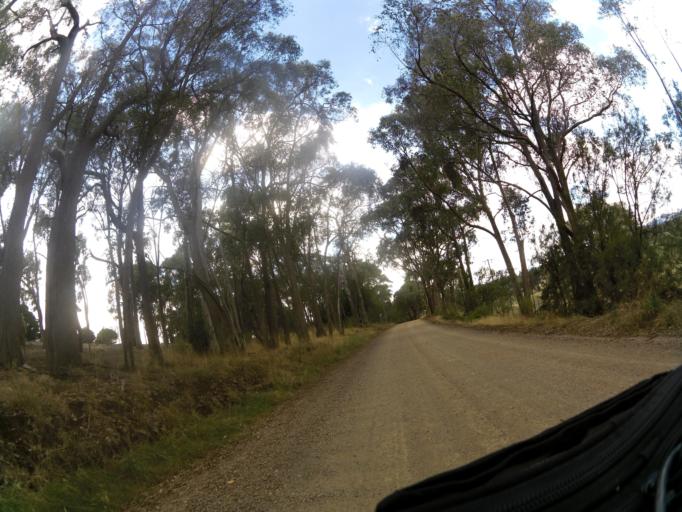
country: AU
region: Victoria
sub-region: Benalla
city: Benalla
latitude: -36.7819
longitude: 145.9912
